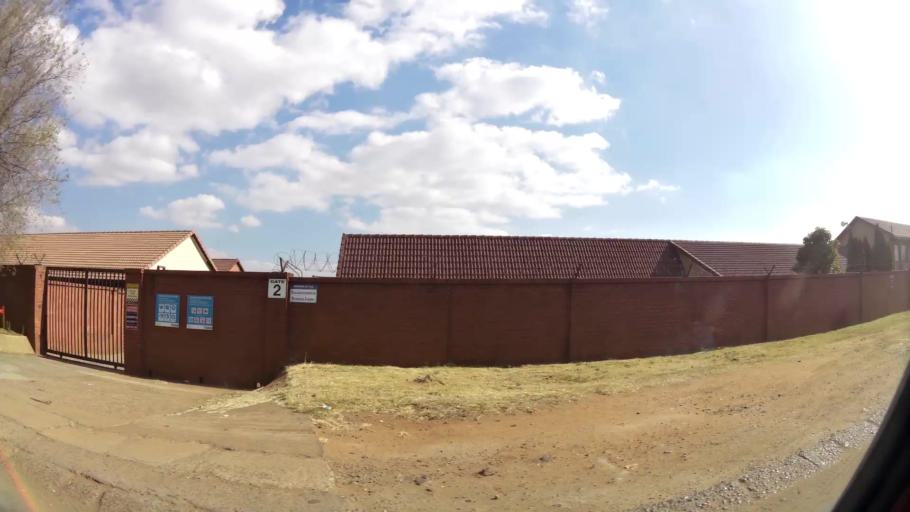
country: ZA
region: Gauteng
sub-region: Ekurhuleni Metropolitan Municipality
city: Tembisa
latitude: -25.9632
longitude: 28.2312
